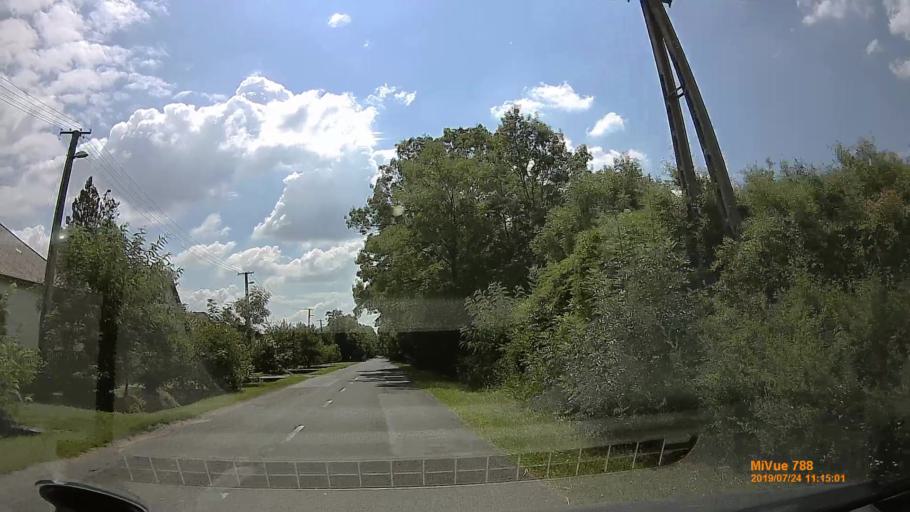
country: HU
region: Szabolcs-Szatmar-Bereg
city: Tarpa
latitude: 48.1947
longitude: 22.4534
